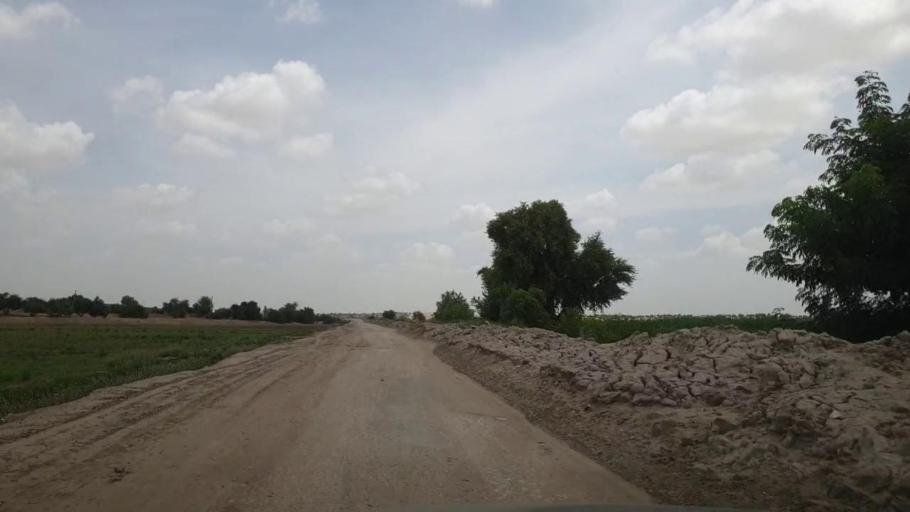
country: PK
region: Sindh
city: Kot Diji
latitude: 27.2034
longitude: 69.1205
